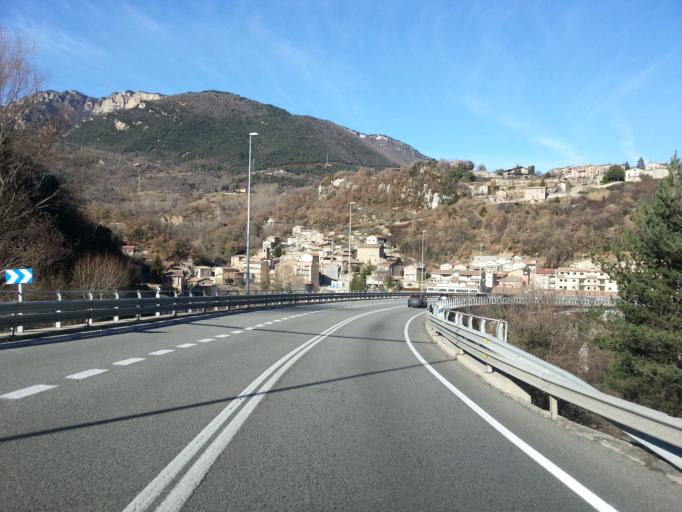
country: ES
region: Catalonia
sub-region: Provincia de Barcelona
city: Berga
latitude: 42.1437
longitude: 1.8631
